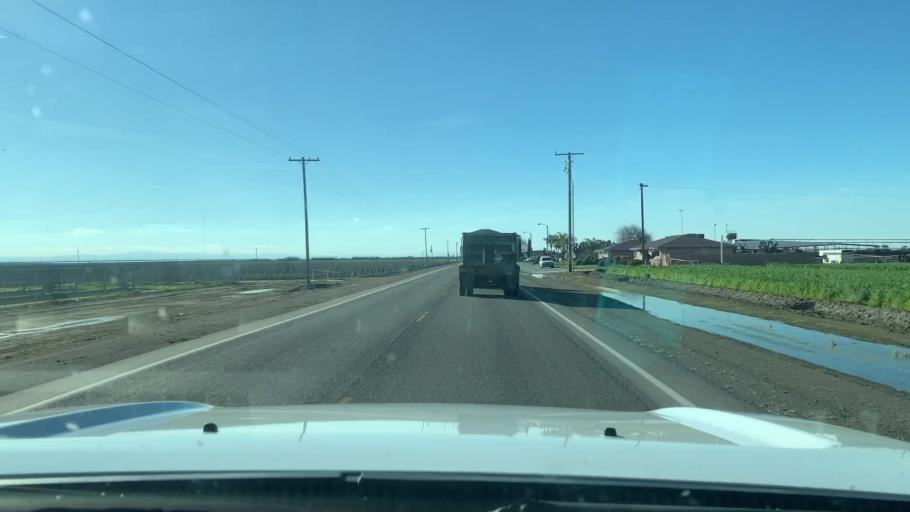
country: US
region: California
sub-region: Kings County
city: Corcoran
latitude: 36.2111
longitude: -119.5417
